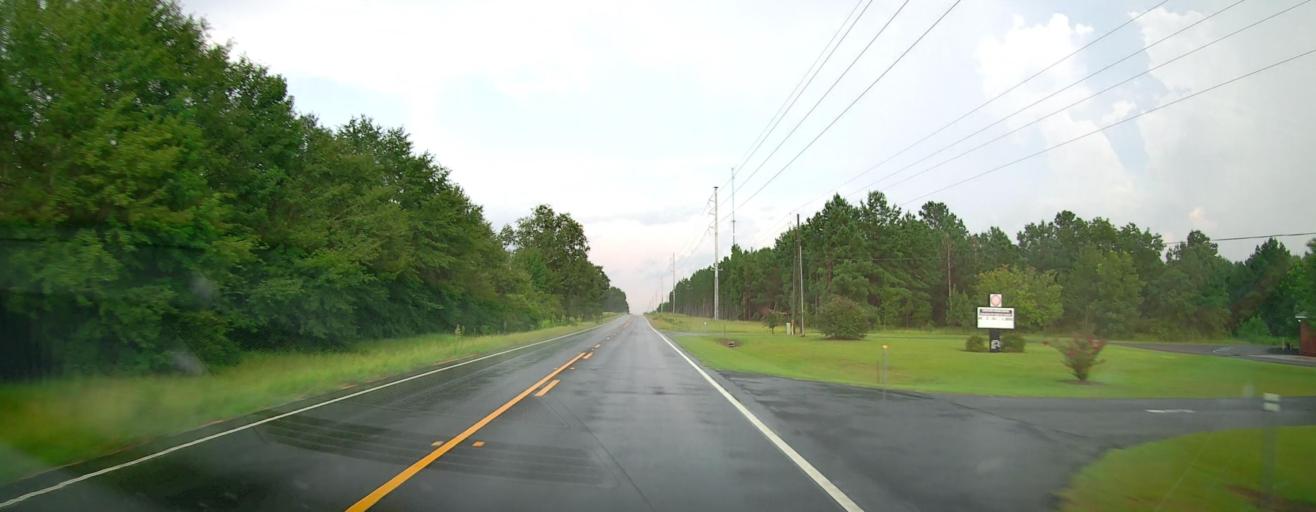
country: US
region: Georgia
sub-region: Dodge County
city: Chester
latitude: 32.5728
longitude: -83.1960
